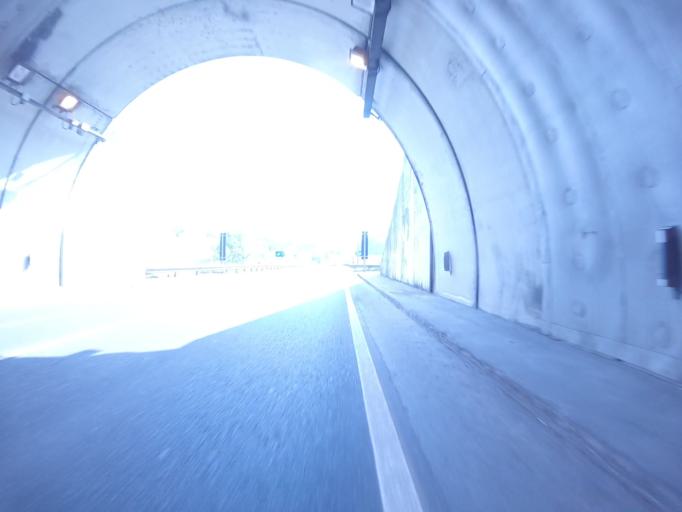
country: ES
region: Basque Country
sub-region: Provincia de Guipuzcoa
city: Azkoitia
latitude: 43.1722
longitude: -2.3075
